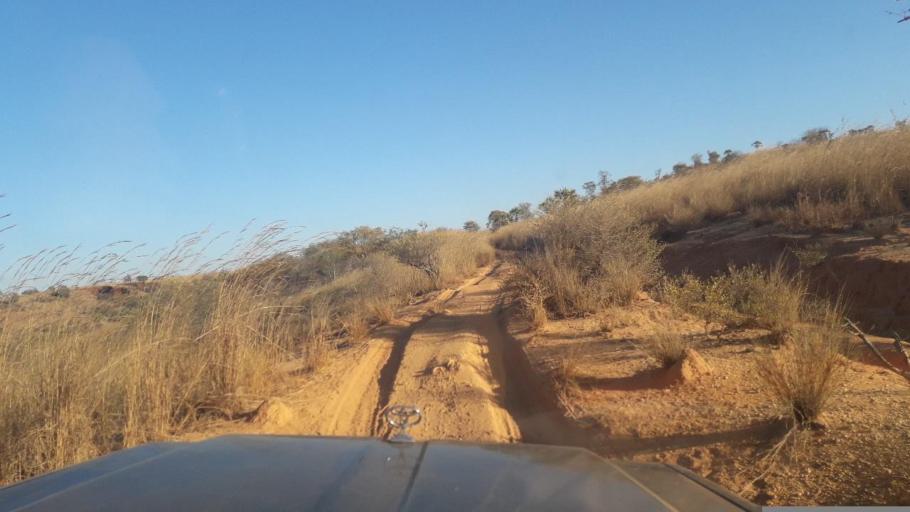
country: MG
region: Boeny
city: Sitampiky
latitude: -16.4952
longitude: 45.6076
